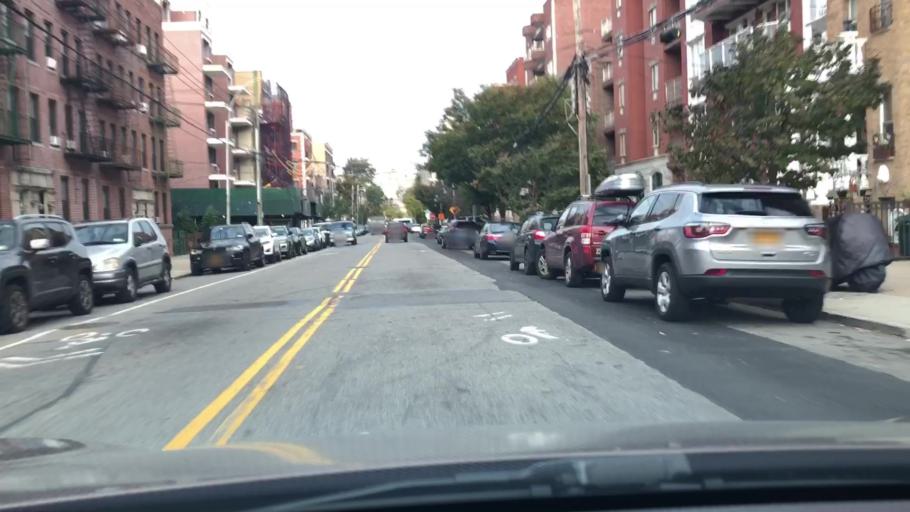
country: US
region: New York
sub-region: Queens County
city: Long Island City
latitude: 40.7662
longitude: -73.9273
